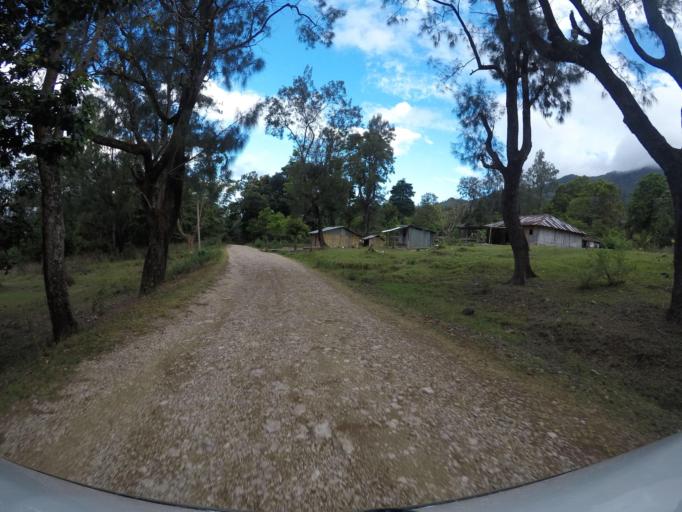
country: TL
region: Baucau
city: Venilale
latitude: -8.6807
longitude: 126.6463
